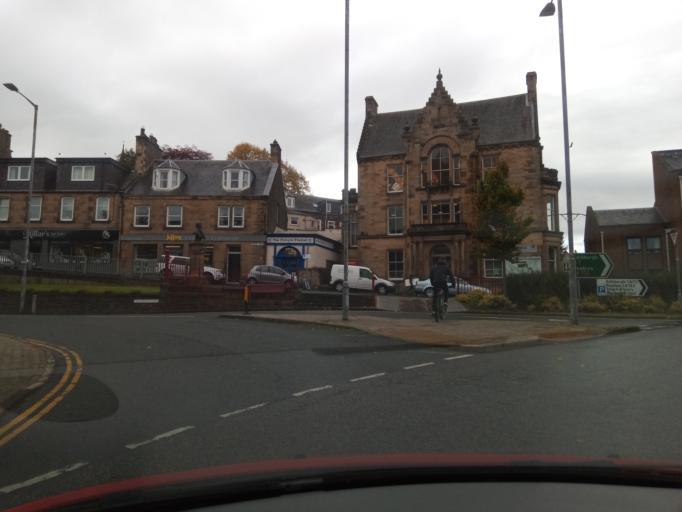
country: GB
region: Scotland
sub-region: The Scottish Borders
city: Galashiels
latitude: 55.6146
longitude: -2.8066
